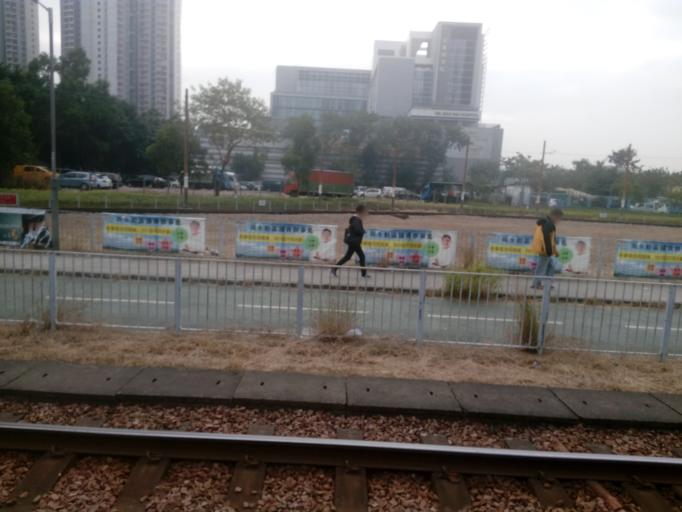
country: HK
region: Yuen Long
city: Yuen Long Kau Hui
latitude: 22.4591
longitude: 113.9977
